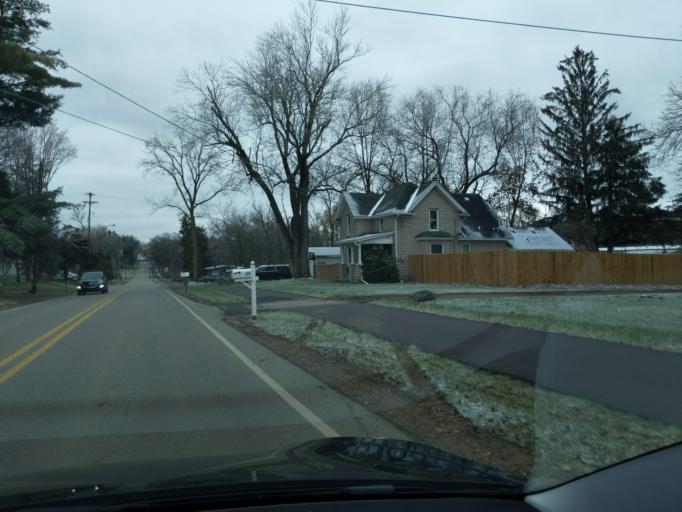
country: US
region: Michigan
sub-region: Jackson County
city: Spring Arbor
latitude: 42.2035
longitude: -84.5538
